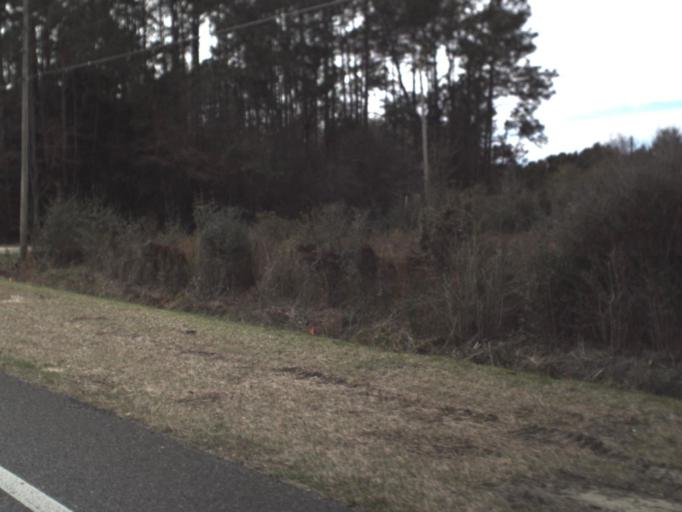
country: US
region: Florida
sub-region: Bay County
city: Youngstown
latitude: 30.3067
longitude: -85.4755
